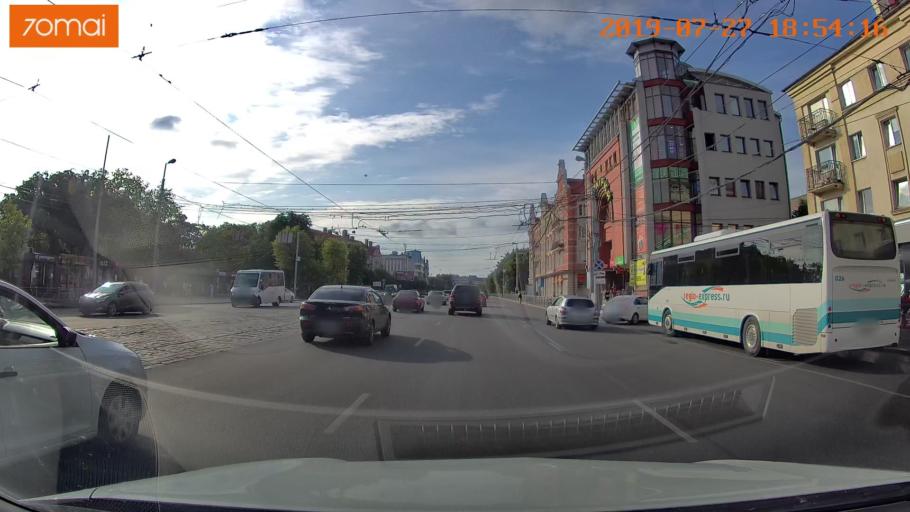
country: RU
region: Kaliningrad
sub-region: Gorod Kaliningrad
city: Kaliningrad
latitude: 54.7122
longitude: 20.5084
